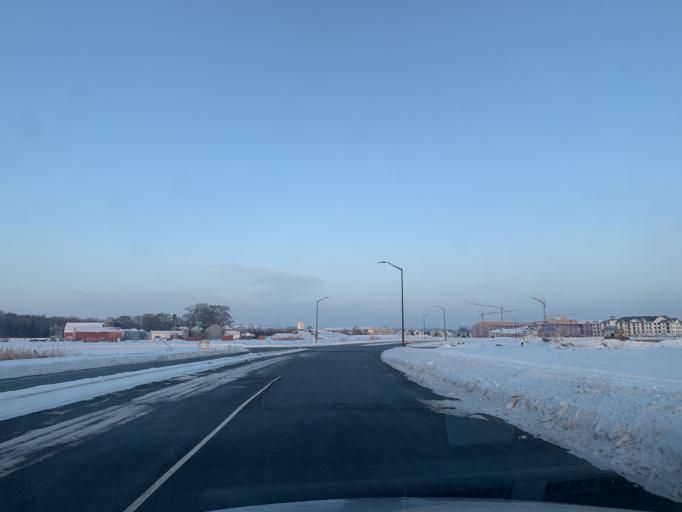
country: US
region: Minnesota
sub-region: Scott County
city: Shakopee
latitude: 44.7862
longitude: -93.4843
